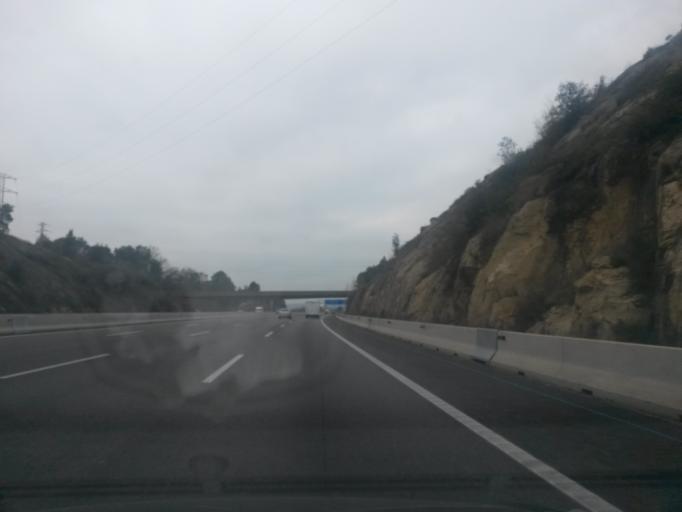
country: ES
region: Catalonia
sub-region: Provincia de Girona
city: Girona
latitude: 42.0030
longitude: 2.8054
